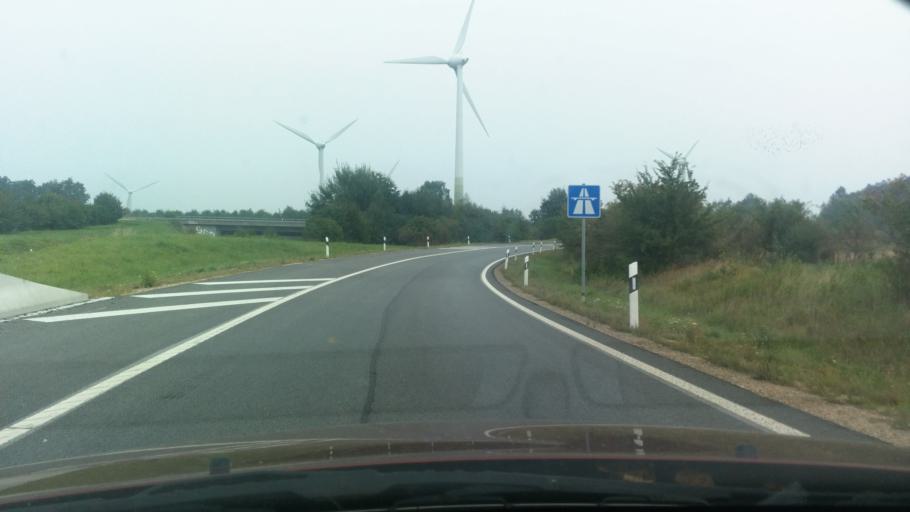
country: DE
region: Saxony
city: Goerlitz
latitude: 51.1961
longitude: 14.9623
